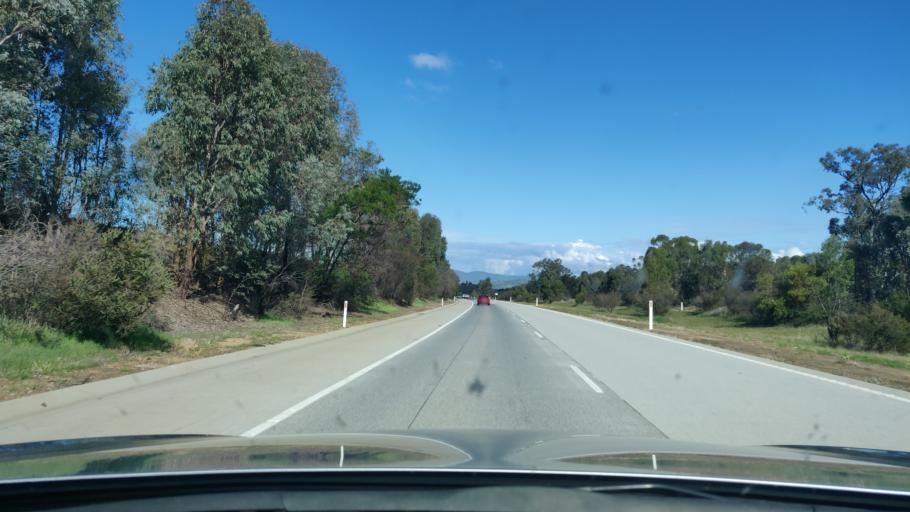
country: AU
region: New South Wales
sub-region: Albury Municipality
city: Lavington
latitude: -36.0307
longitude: 146.9771
